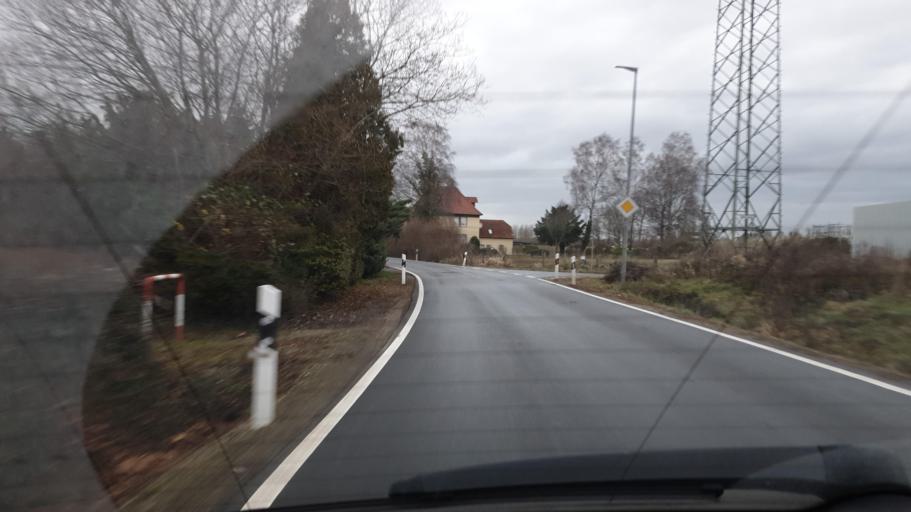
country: DE
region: North Rhine-Westphalia
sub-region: Regierungsbezirk Detmold
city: Lage
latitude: 51.9855
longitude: 8.8441
